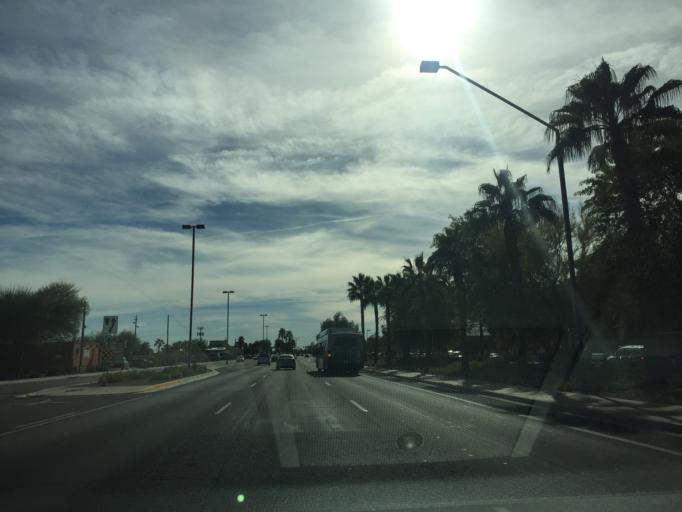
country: US
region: Arizona
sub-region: Maricopa County
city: Gilbert
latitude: 33.3400
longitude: -111.7899
